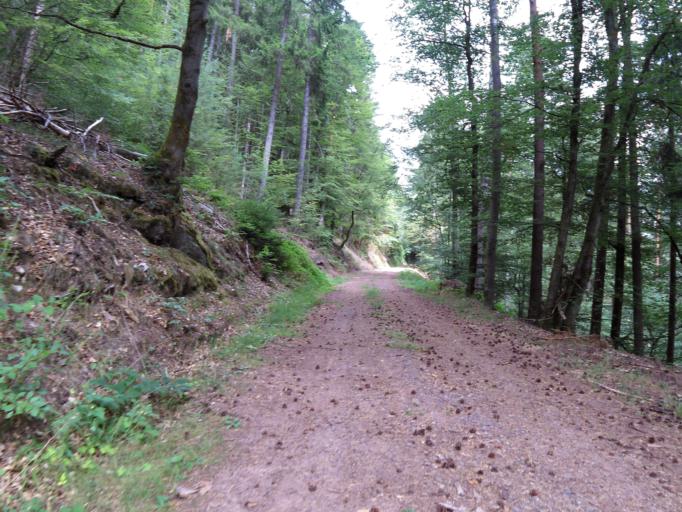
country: DE
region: Rheinland-Pfalz
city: Elmstein
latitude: 49.3669
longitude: 7.9273
